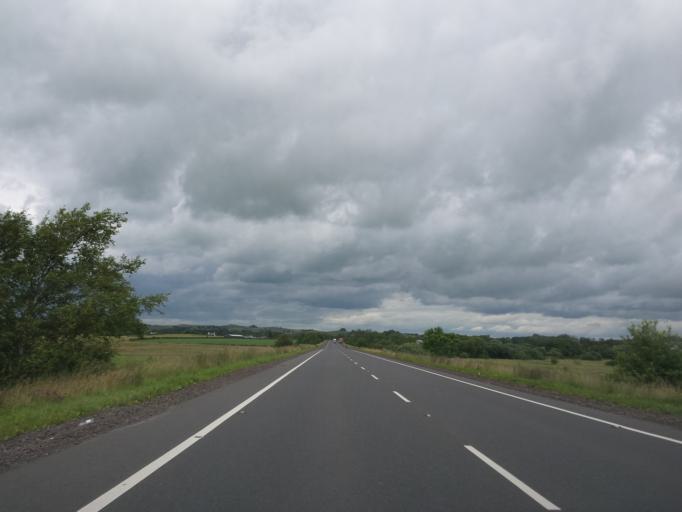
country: GB
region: Scotland
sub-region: Dumfries and Galloway
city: Castle Douglas
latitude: 54.9343
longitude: -3.9488
